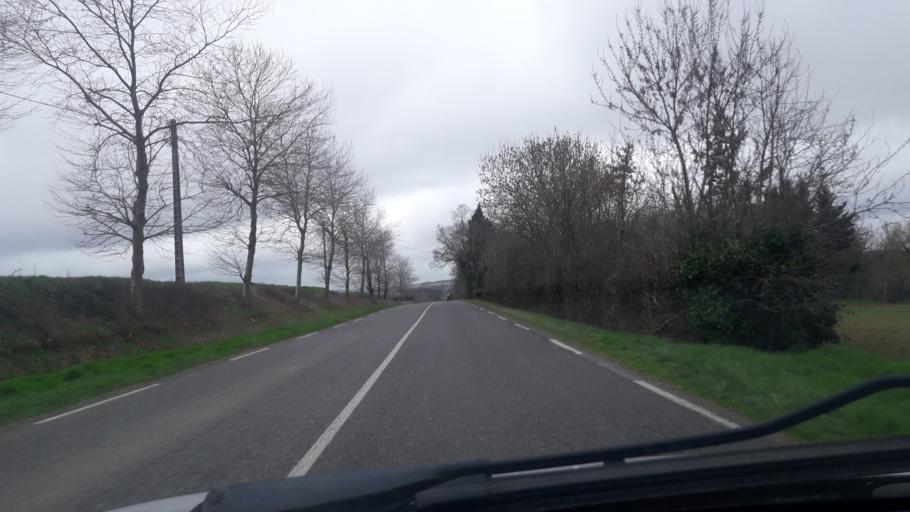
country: FR
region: Midi-Pyrenees
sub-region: Departement du Gers
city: Gimont
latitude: 43.6665
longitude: 1.0176
